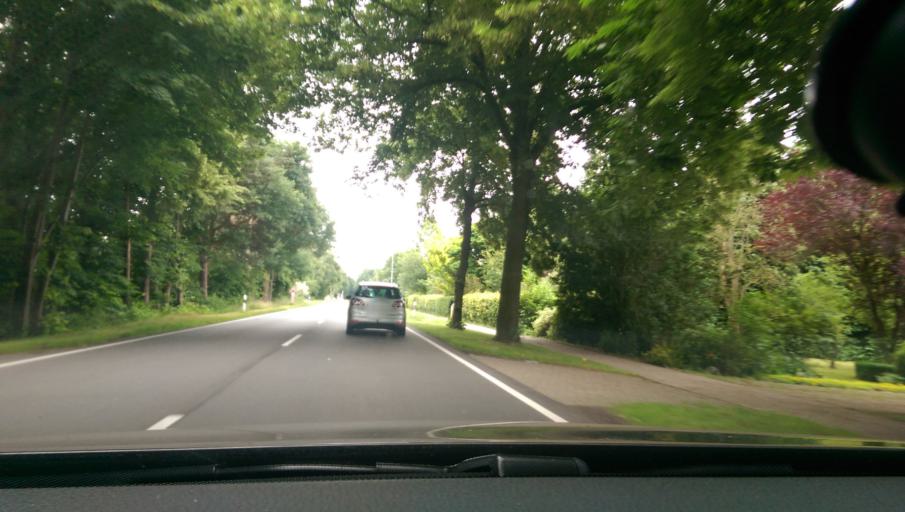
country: DE
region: Lower Saxony
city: Botersen
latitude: 53.1679
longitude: 9.3033
